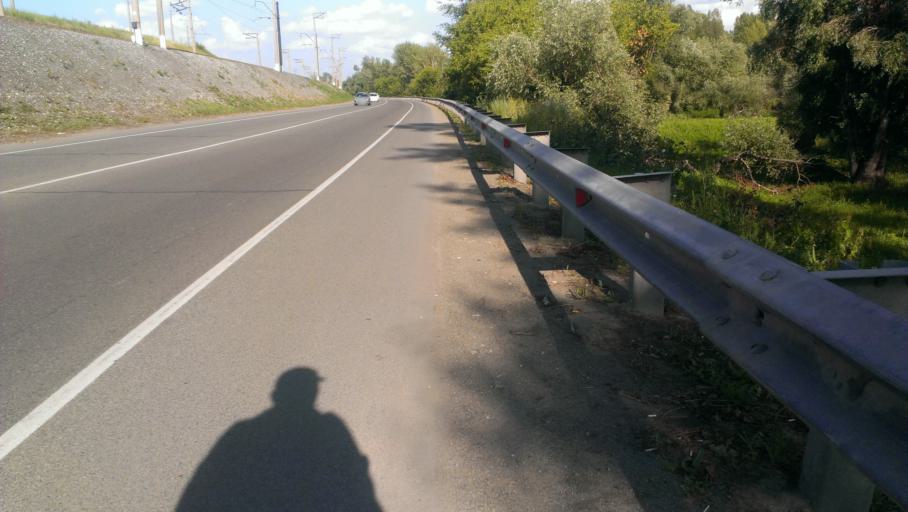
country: RU
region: Altai Krai
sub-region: Gorod Barnaulskiy
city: Barnaul
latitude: 53.3669
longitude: 83.8417
